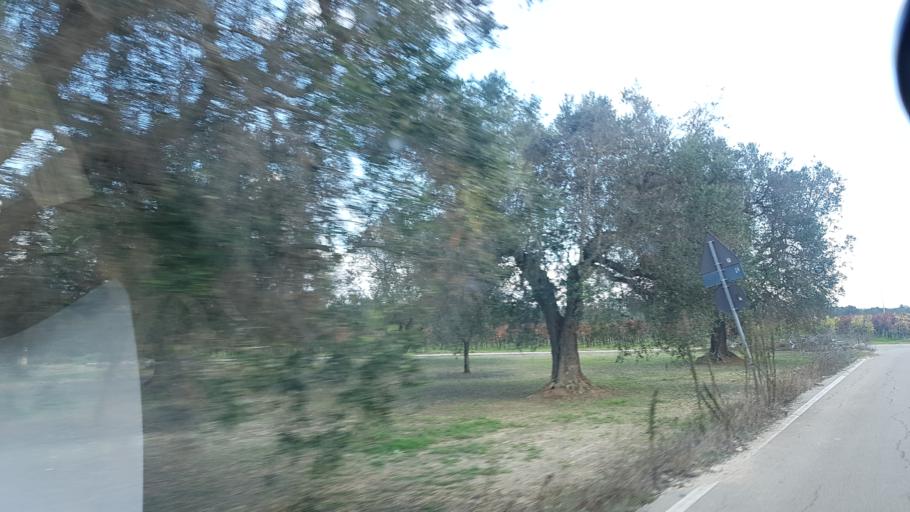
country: IT
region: Apulia
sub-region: Provincia di Brindisi
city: San Pietro Vernotico
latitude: 40.5094
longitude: 18.0204
